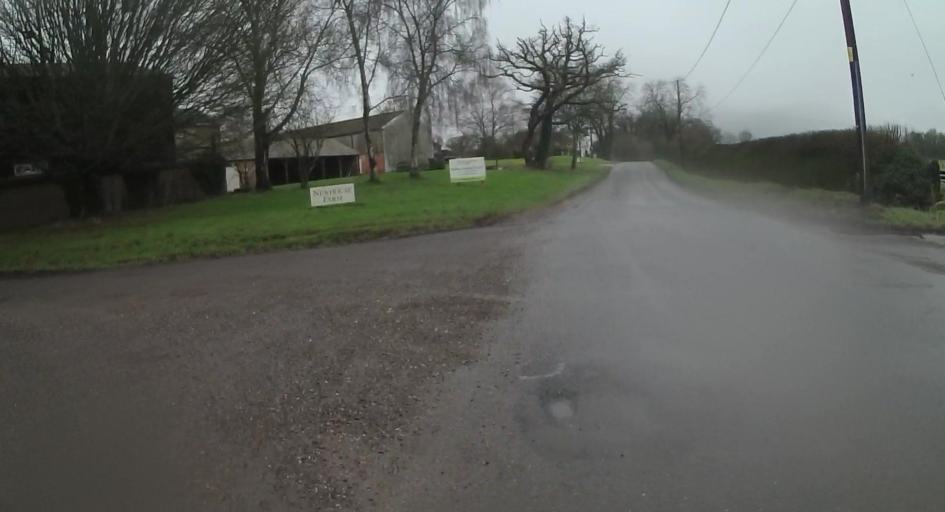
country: GB
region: England
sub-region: Hampshire
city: Kings Worthy
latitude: 51.1281
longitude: -1.2205
